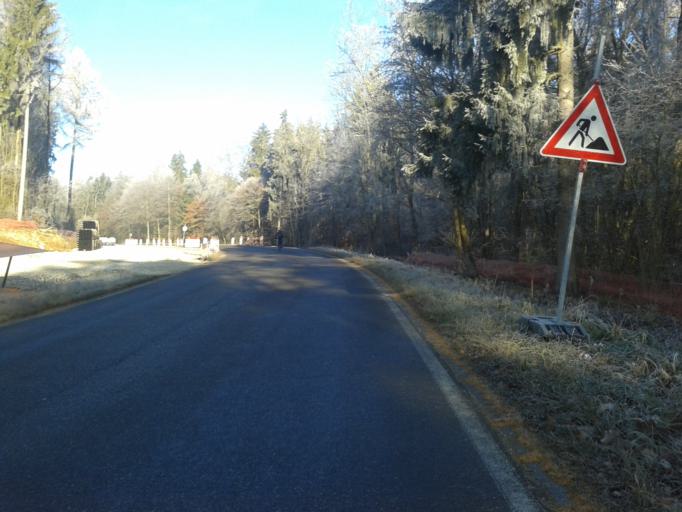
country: DE
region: Baden-Wuerttemberg
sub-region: Tuebingen Region
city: Ulm
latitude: 48.4178
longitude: 9.9634
